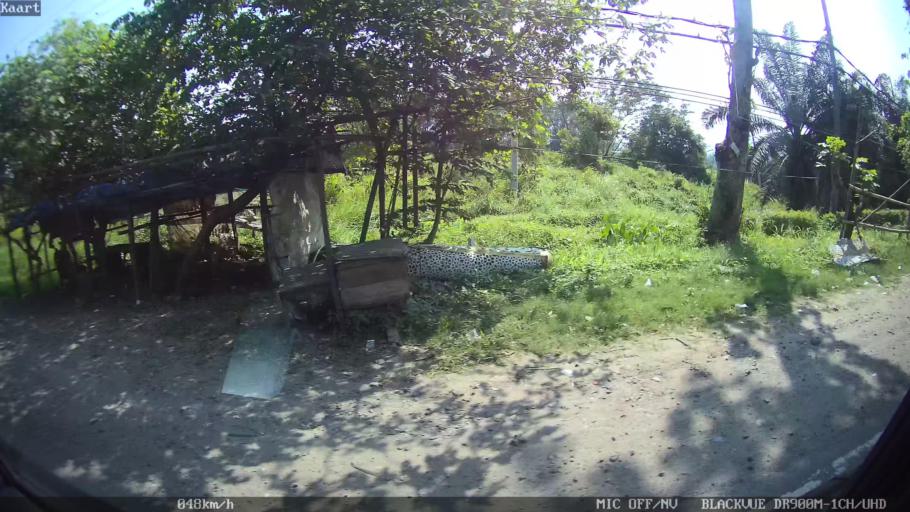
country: ID
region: Lampung
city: Natar
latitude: -5.3350
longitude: 105.2097
